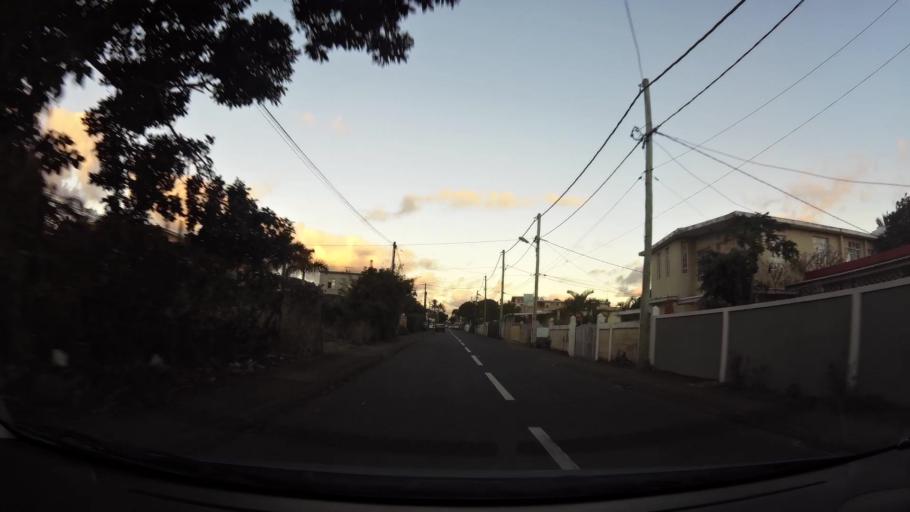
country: MU
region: Moka
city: Saint Pierre
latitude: -20.2165
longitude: 57.5282
